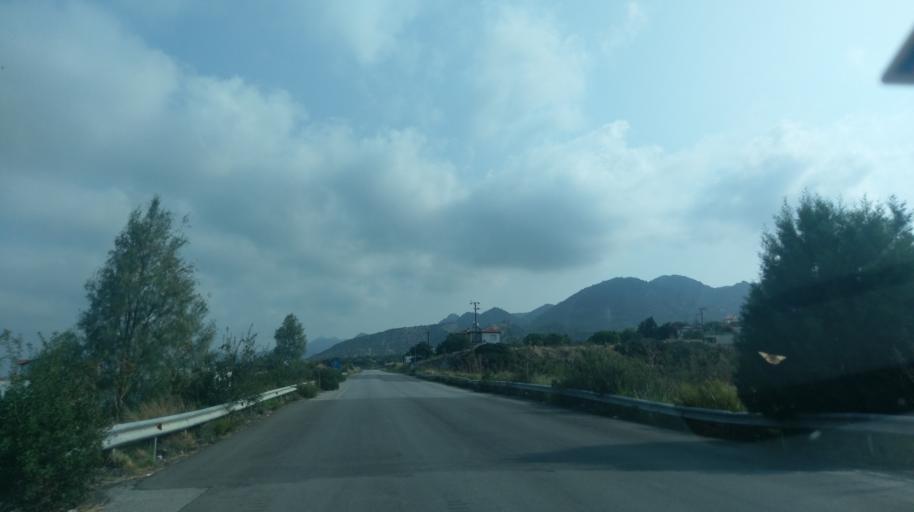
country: CY
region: Ammochostos
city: Lefkonoiko
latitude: 35.3538
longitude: 33.6377
